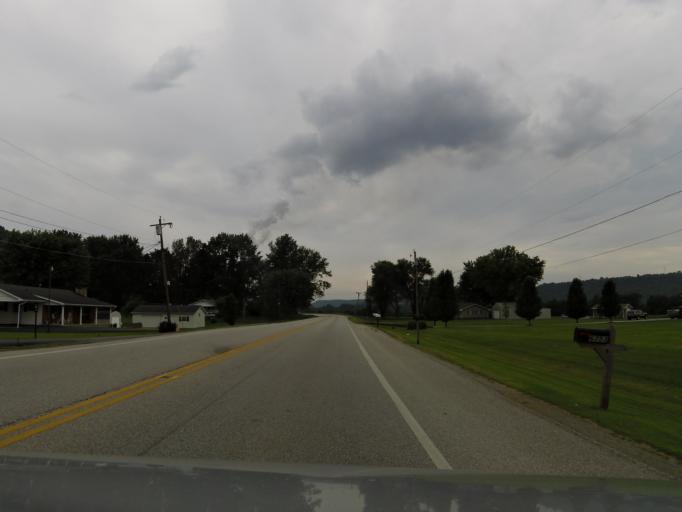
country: US
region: Ohio
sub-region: Brown County
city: Ripley
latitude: 38.7166
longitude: -83.8236
